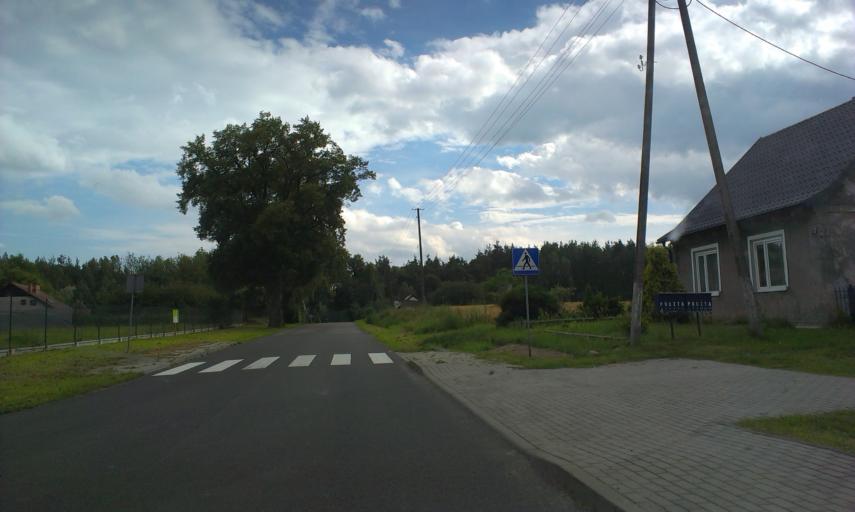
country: PL
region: Greater Poland Voivodeship
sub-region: Powiat zlotowski
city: Zlotow
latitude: 53.4415
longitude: 16.9847
